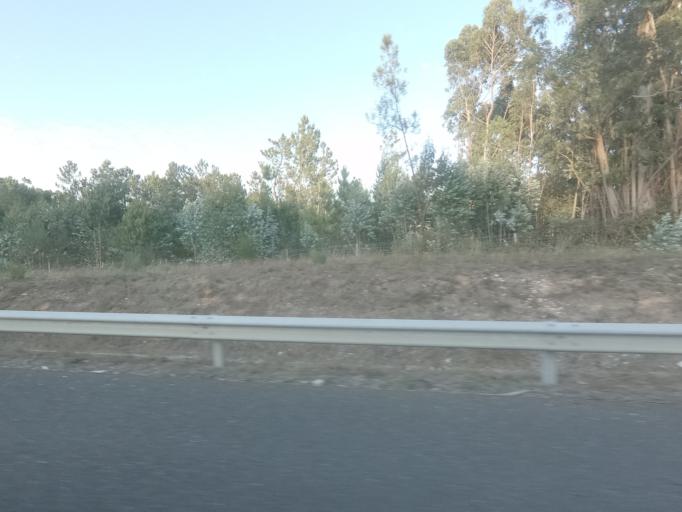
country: PT
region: Santarem
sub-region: Ourem
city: Fatima
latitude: 39.6283
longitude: -8.6973
